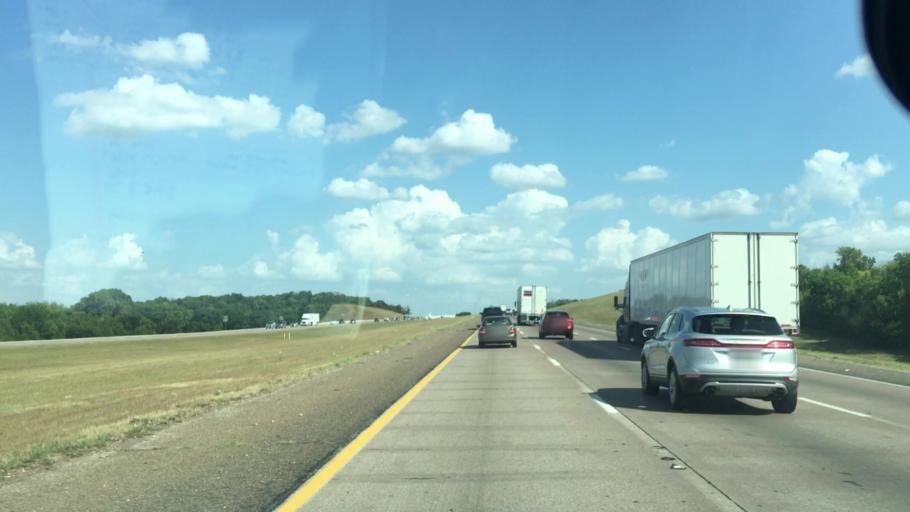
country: US
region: Texas
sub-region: Dallas County
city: Hutchins
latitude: 32.6733
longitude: -96.7373
